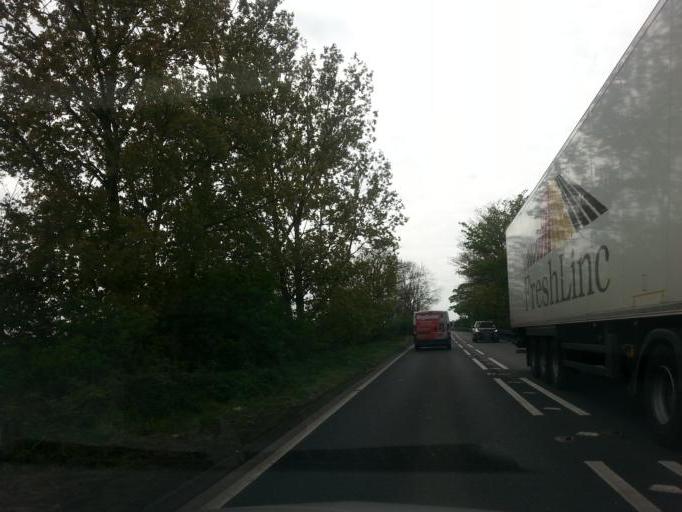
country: GB
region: England
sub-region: Cambridgeshire
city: March
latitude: 52.6239
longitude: 0.0887
